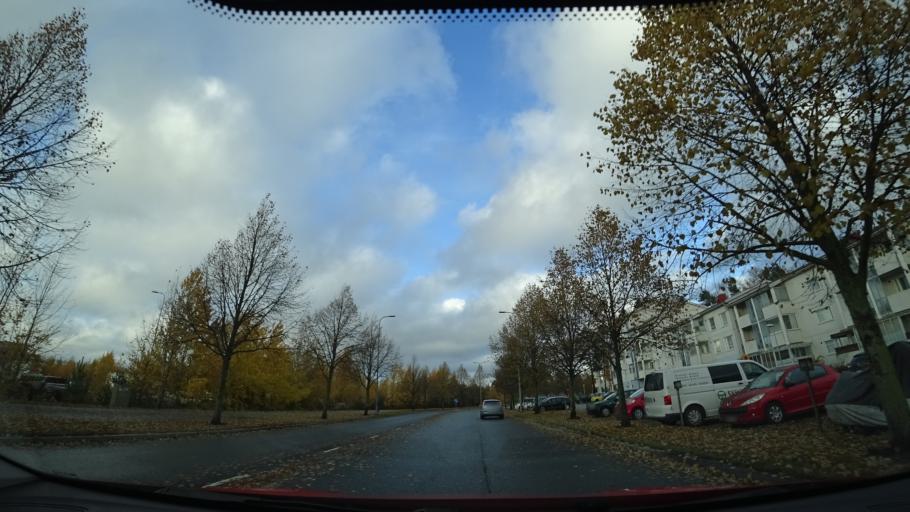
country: FI
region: Uusimaa
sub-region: Helsinki
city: Vantaa
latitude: 60.2964
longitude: 25.0494
